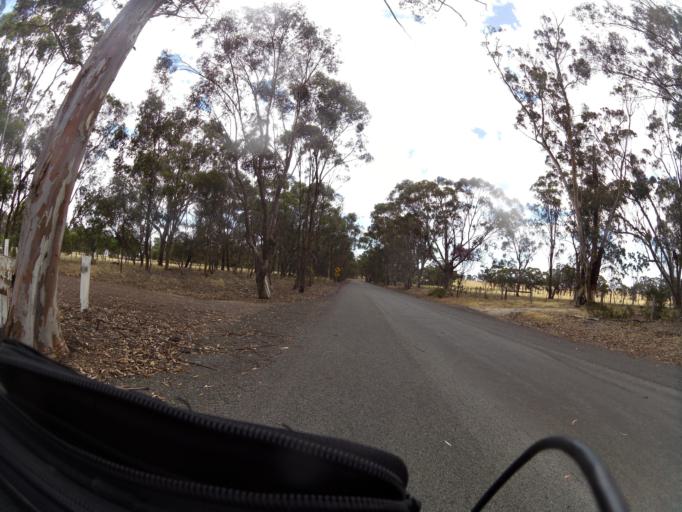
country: AU
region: Victoria
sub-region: Greater Shepparton
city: Shepparton
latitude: -36.7316
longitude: 145.1514
